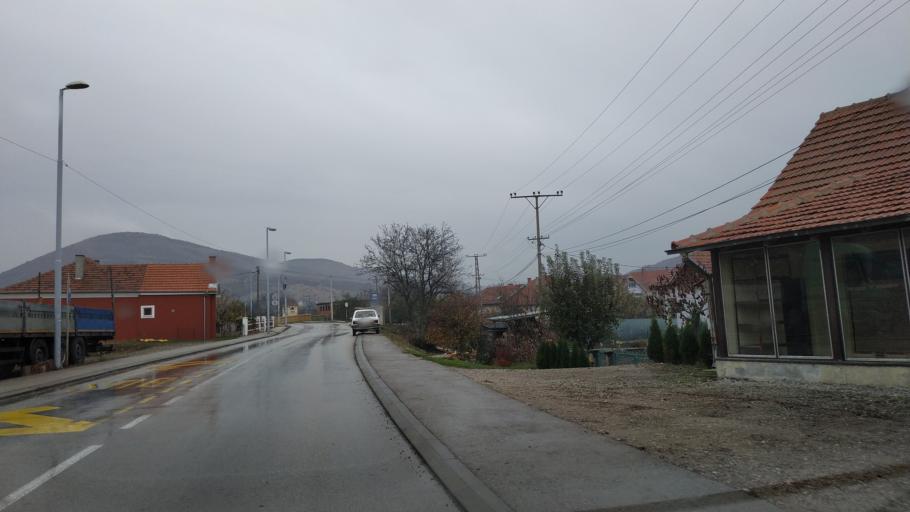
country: RS
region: Central Serbia
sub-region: Pirotski Okrug
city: Dimitrovgrad
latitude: 43.0119
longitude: 22.7519
